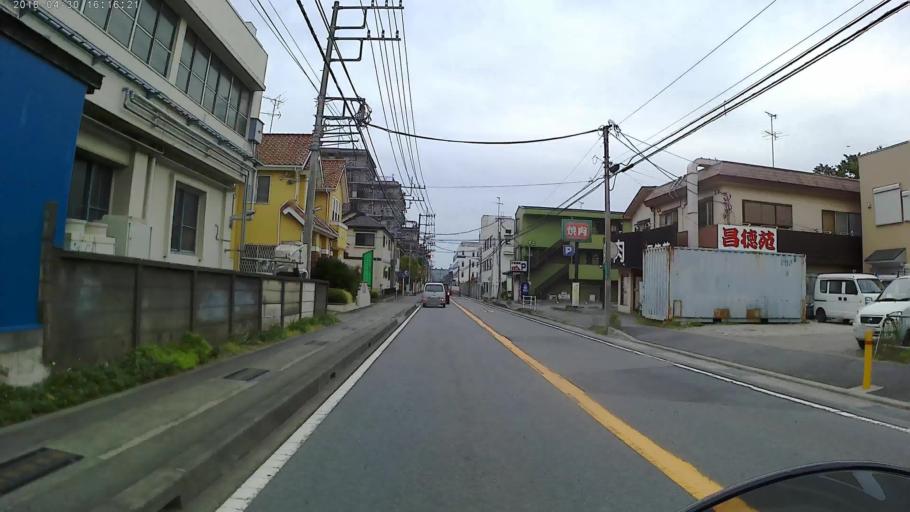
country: JP
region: Kanagawa
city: Minami-rinkan
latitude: 35.4833
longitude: 139.4317
